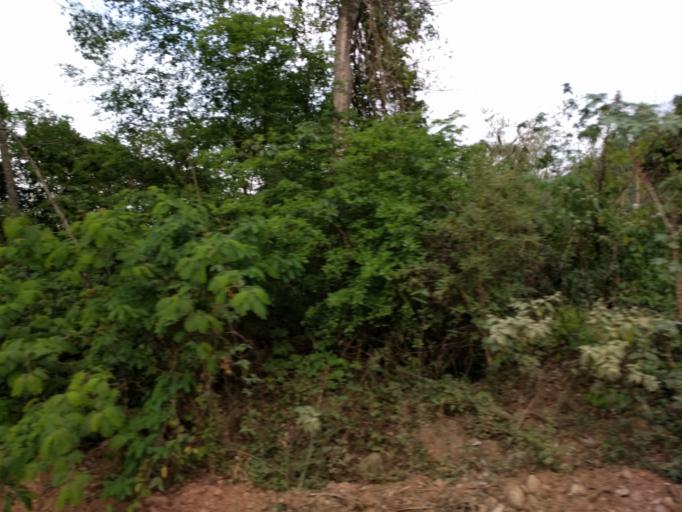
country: BO
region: Santa Cruz
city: Santa Rita
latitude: -17.9296
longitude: -63.3913
